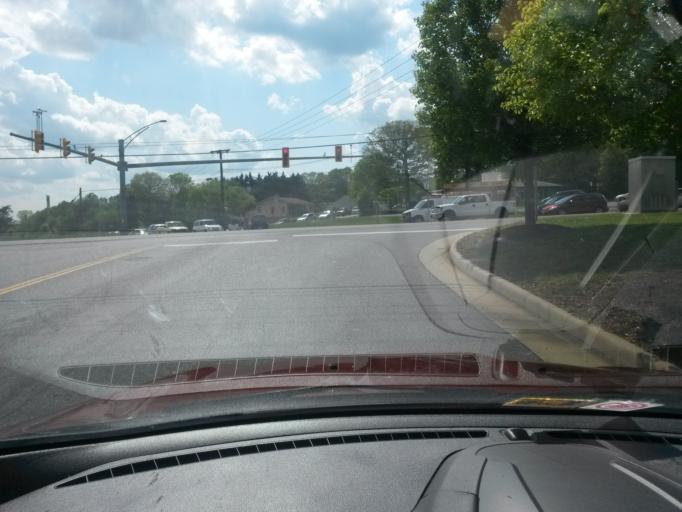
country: US
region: Virginia
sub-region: Campbell County
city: Timberlake
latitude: 37.3188
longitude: -79.1884
